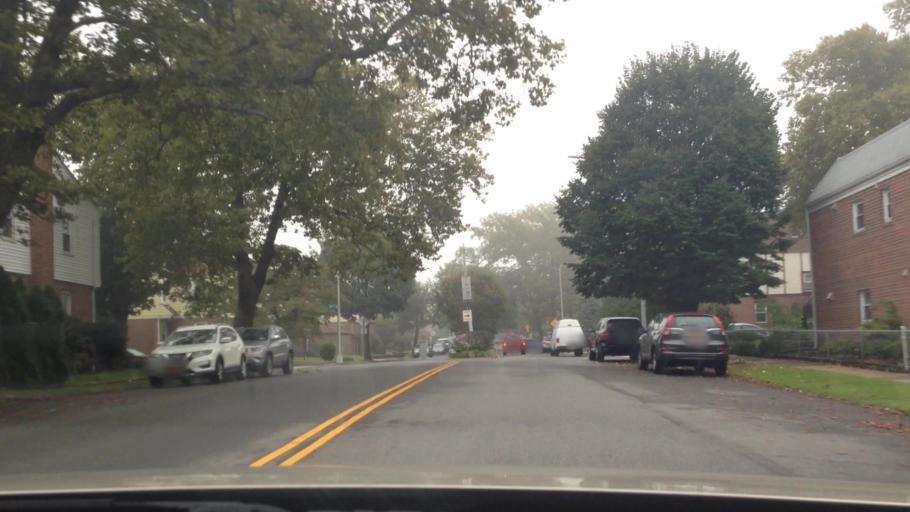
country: US
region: New York
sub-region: Nassau County
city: East Atlantic Beach
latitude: 40.7466
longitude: -73.7861
